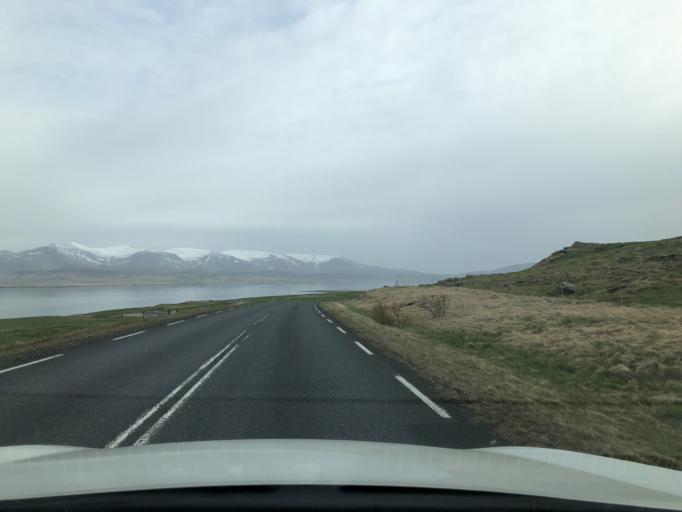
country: IS
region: Capital Region
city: Mosfellsbaer
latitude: 64.3251
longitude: -21.7478
